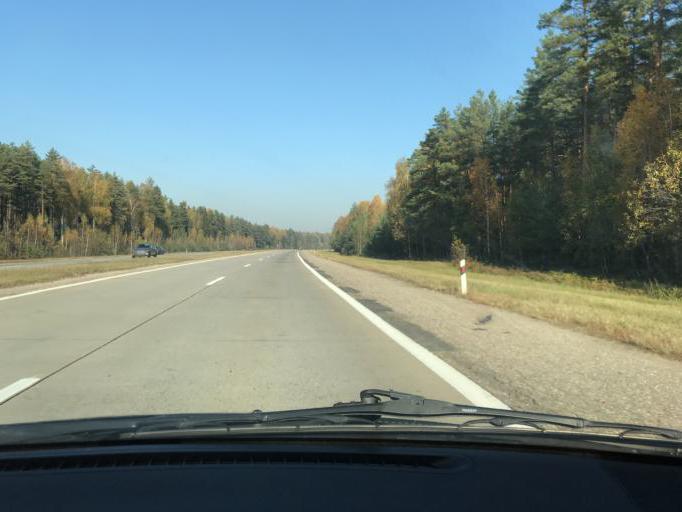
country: BY
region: Minsk
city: Uzda
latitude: 53.4028
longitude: 27.4811
